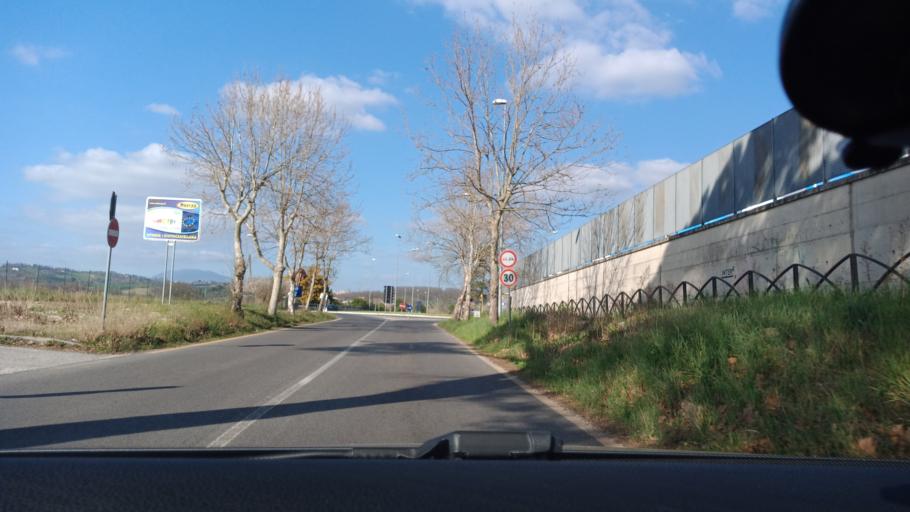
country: IT
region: Latium
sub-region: Citta metropolitana di Roma Capitale
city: Torrita Tiberina
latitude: 42.2541
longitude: 12.6379
